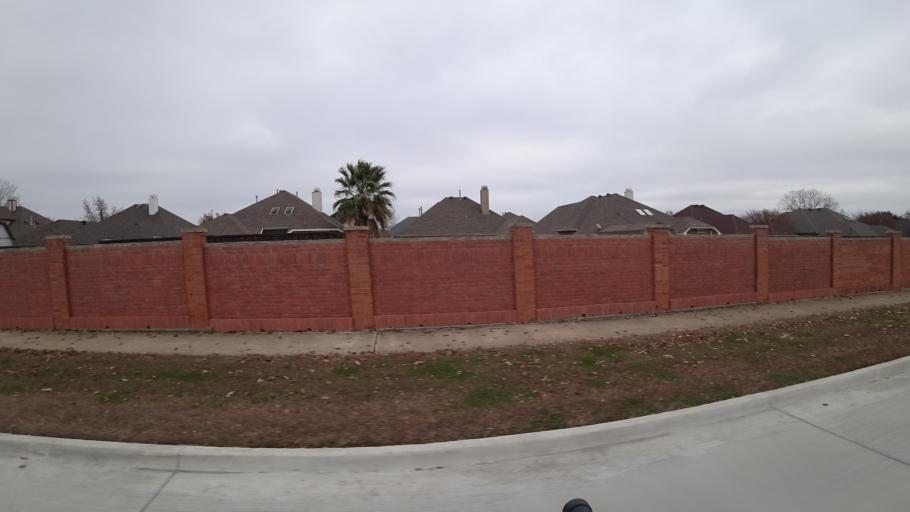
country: US
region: Texas
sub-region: Denton County
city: Lewisville
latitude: 33.0561
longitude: -97.0301
